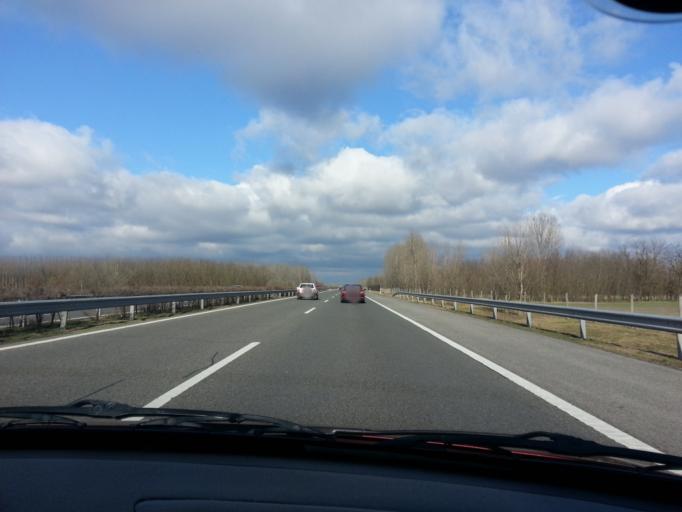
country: HU
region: Csongrad
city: Kistelek
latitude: 46.4863
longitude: 19.9193
